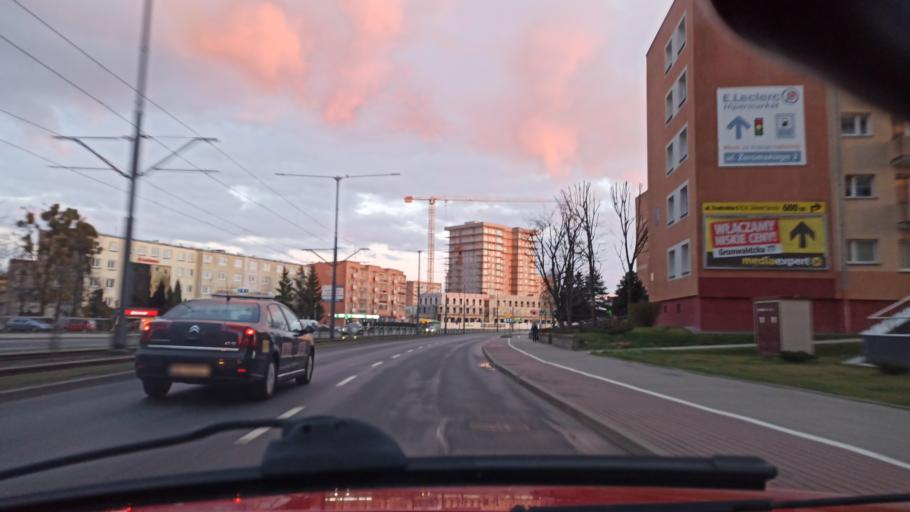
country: PL
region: Warmian-Masurian Voivodeship
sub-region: Powiat elblaski
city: Elblag
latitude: 54.1689
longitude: 19.4053
